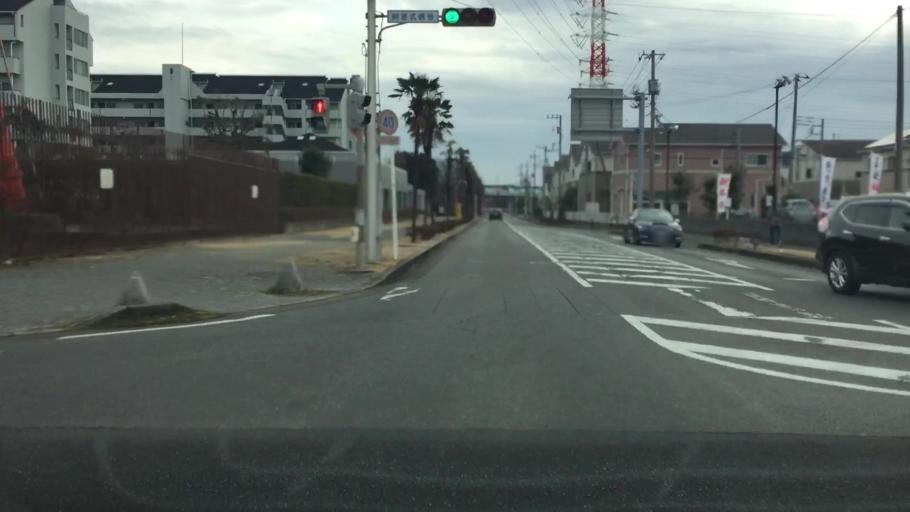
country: JP
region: Chiba
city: Shiroi
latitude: 35.8031
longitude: 140.1285
